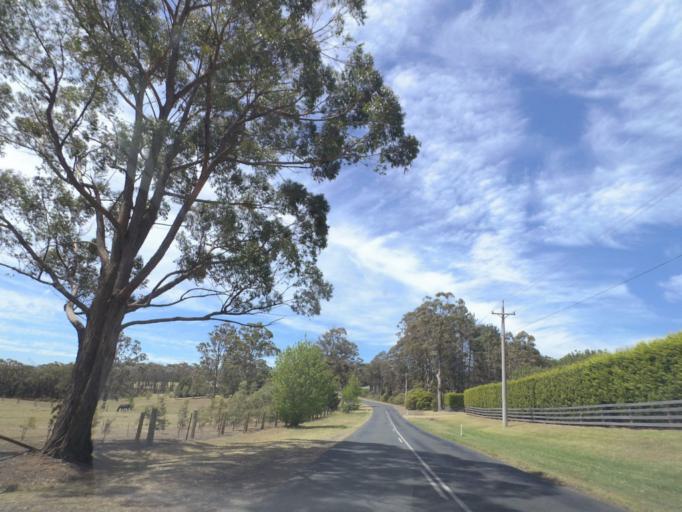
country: AU
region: New South Wales
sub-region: Wingecarribee
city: Colo Vale
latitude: -34.4079
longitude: 150.5269
